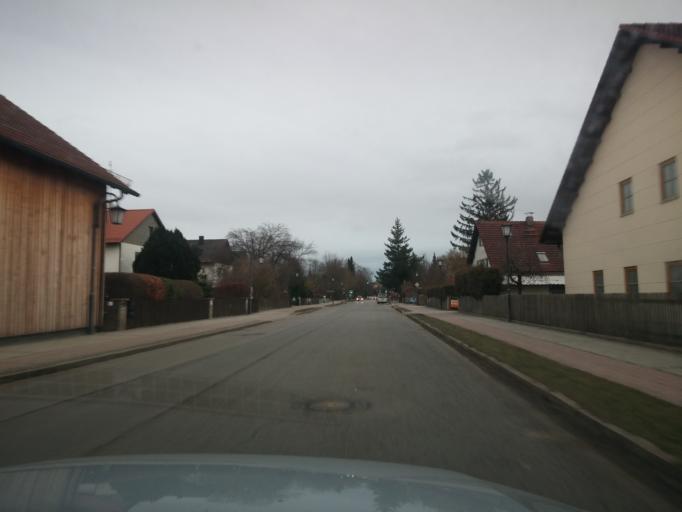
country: DE
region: Bavaria
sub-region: Upper Bavaria
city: Aschheim
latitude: 48.1769
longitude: 11.7128
